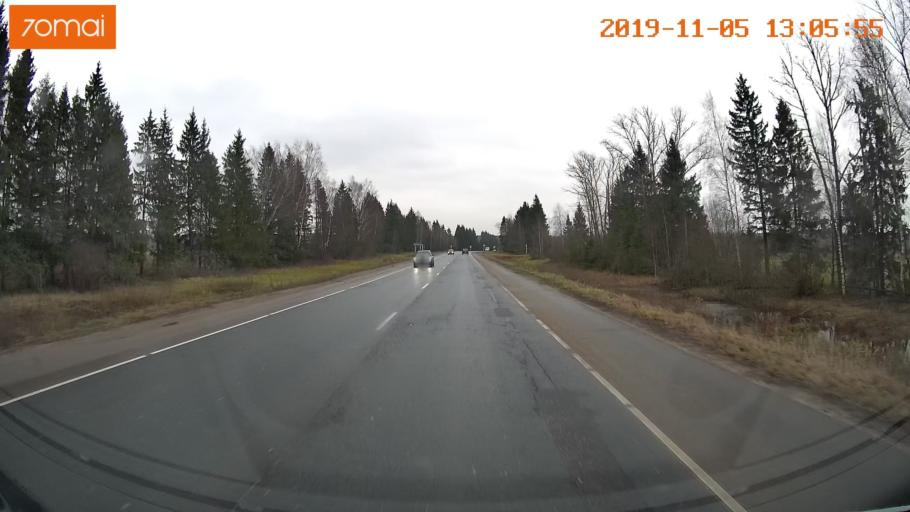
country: RU
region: Ivanovo
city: Kitovo
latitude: 56.8794
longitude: 41.2534
